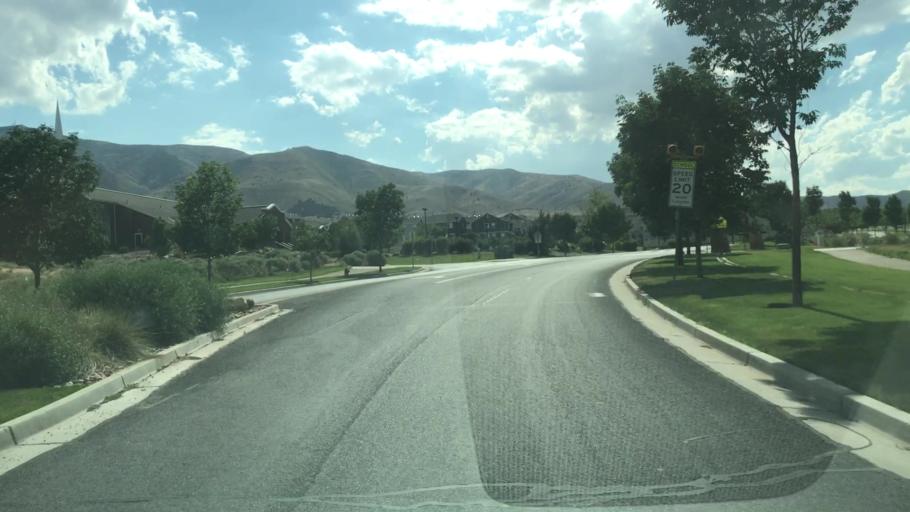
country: US
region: Utah
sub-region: Utah County
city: Saratoga Springs
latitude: 40.3093
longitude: -111.8939
